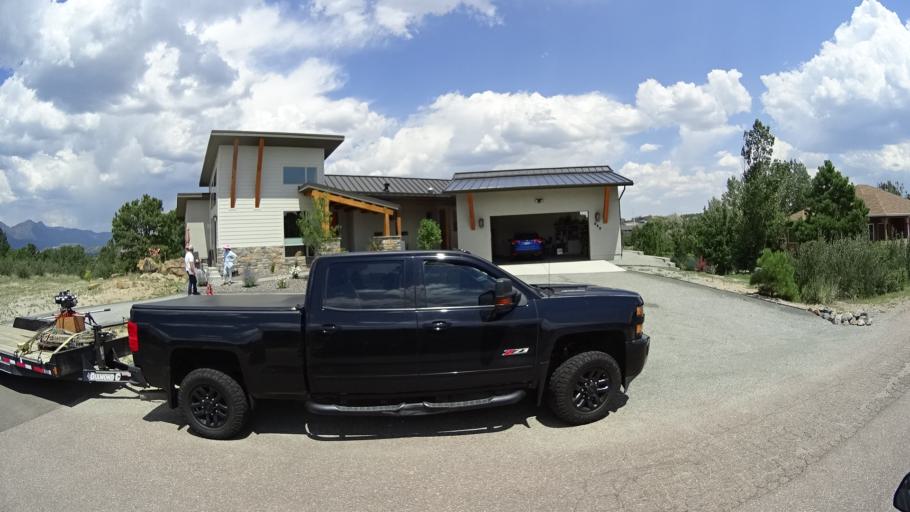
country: US
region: Colorado
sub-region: El Paso County
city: Air Force Academy
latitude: 38.9412
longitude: -104.8073
